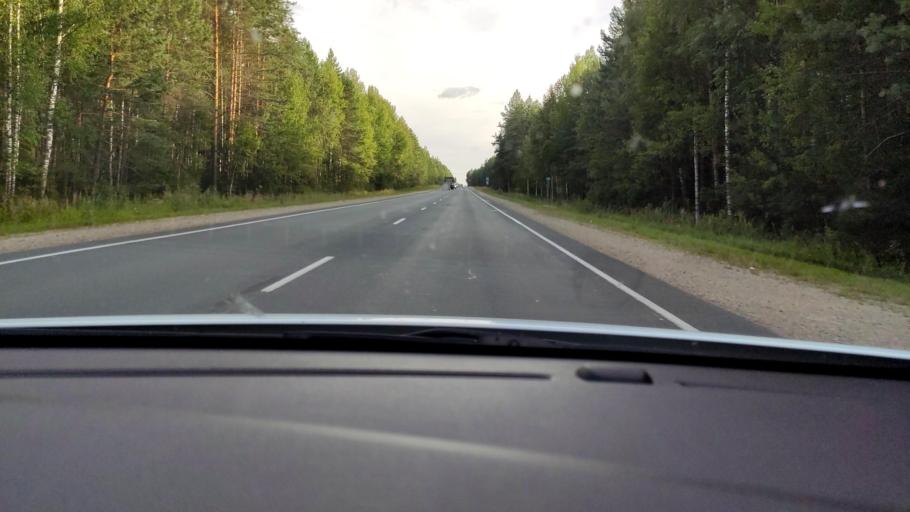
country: RU
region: Mariy-El
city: Suslonger
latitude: 56.2643
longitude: 48.2327
